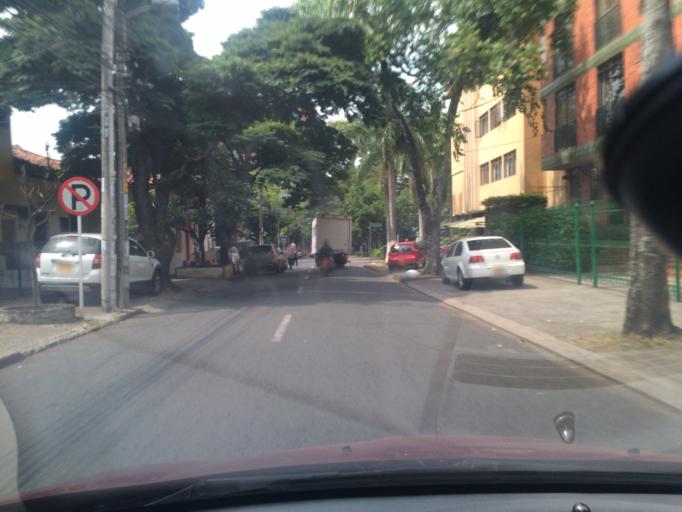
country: CO
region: Valle del Cauca
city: Cali
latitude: 3.4327
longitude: -76.5449
